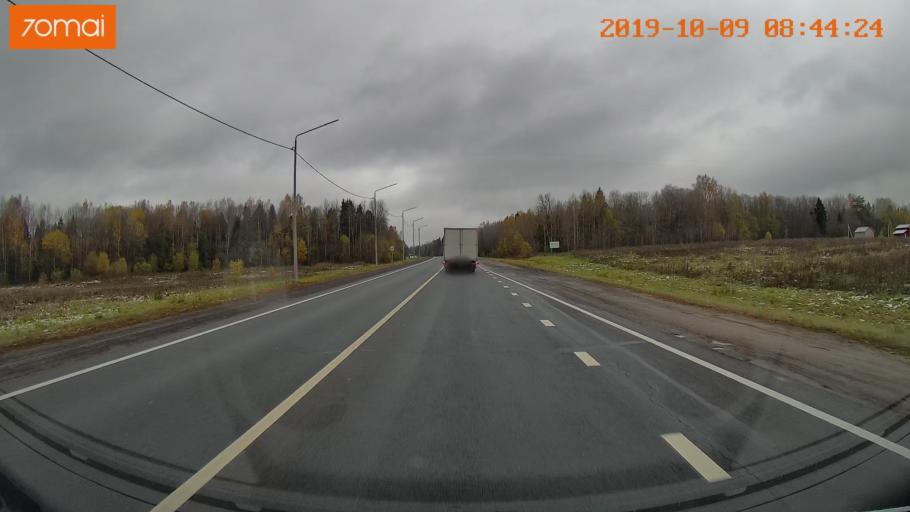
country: RU
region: Vologda
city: Gryazovets
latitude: 59.0363
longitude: 40.1080
